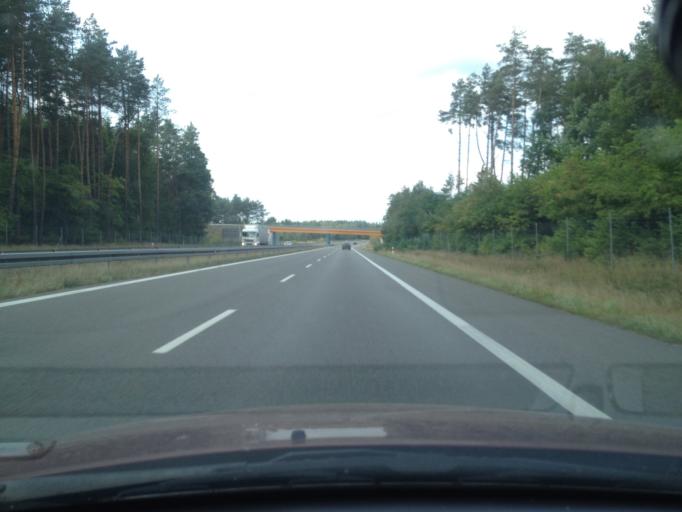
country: PL
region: West Pomeranian Voivodeship
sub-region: Powiat goleniowski
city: Goleniow
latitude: 53.6091
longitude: 14.8204
